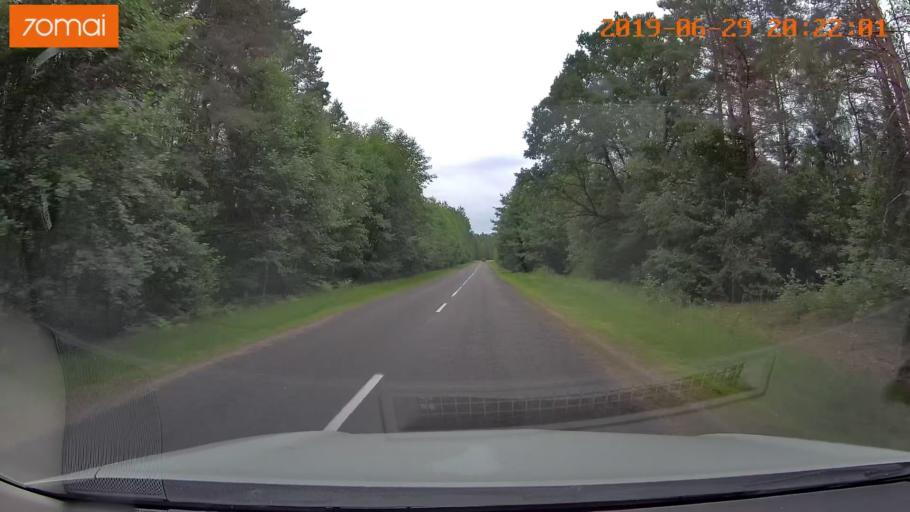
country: BY
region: Brest
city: Asnyezhytsy
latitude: 52.4266
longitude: 26.2535
